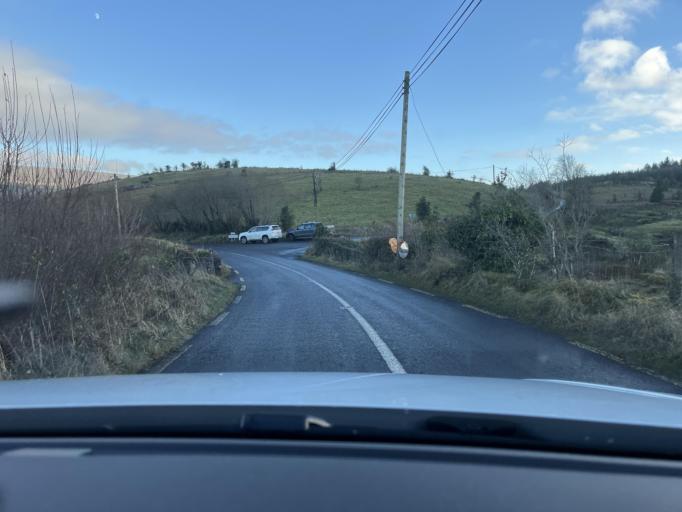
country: IE
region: Connaught
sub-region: County Leitrim
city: Manorhamilton
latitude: 54.1911
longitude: -7.9140
